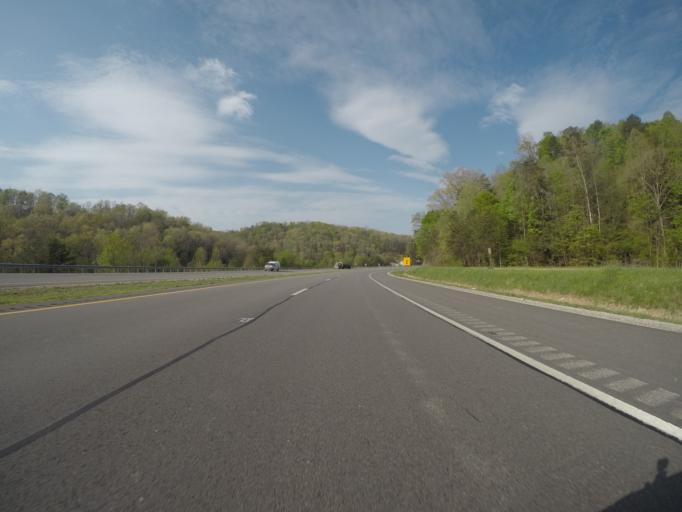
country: US
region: West Virginia
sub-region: Kanawha County
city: Alum Creek
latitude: 38.2813
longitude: -81.7660
